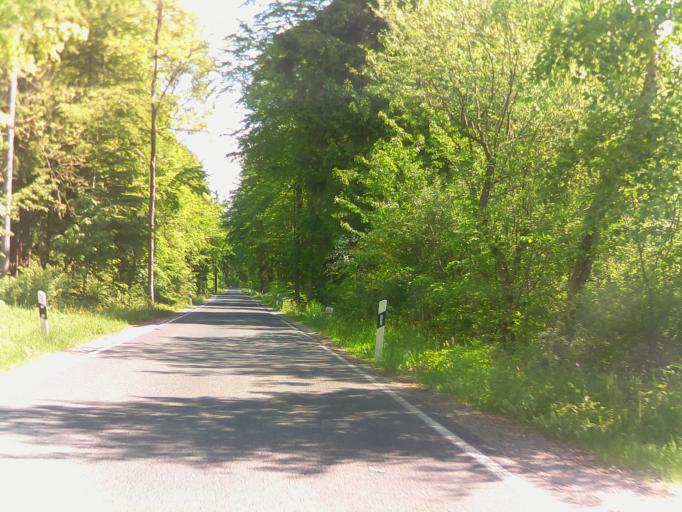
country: DE
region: Thuringia
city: Schmeheim
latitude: 50.5821
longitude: 10.5770
